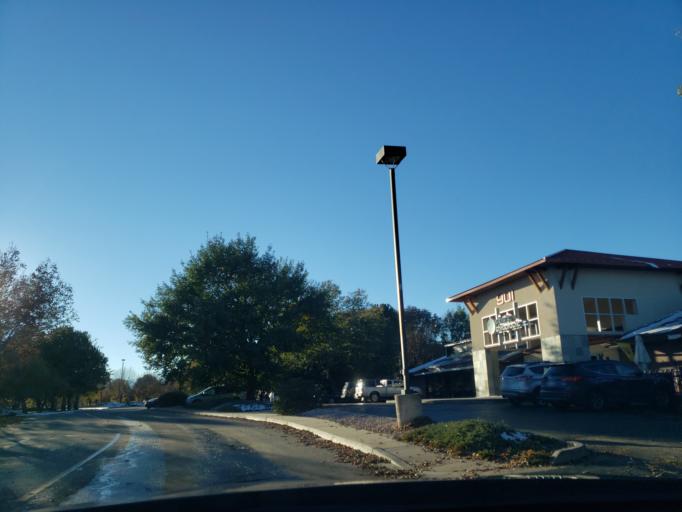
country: US
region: Colorado
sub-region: Larimer County
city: Fort Collins
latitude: 40.5229
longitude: -105.0611
